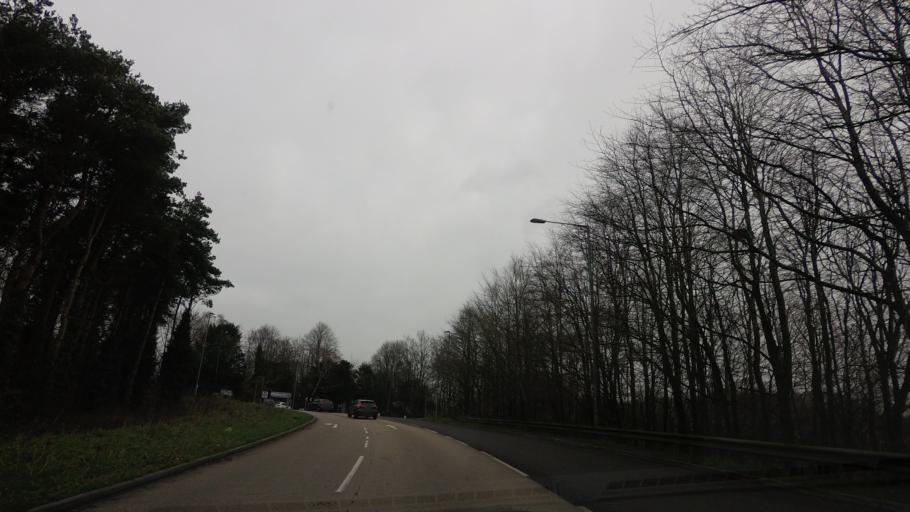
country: GB
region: England
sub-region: East Sussex
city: Saint Leonards-on-Sea
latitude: 50.8907
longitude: 0.5481
